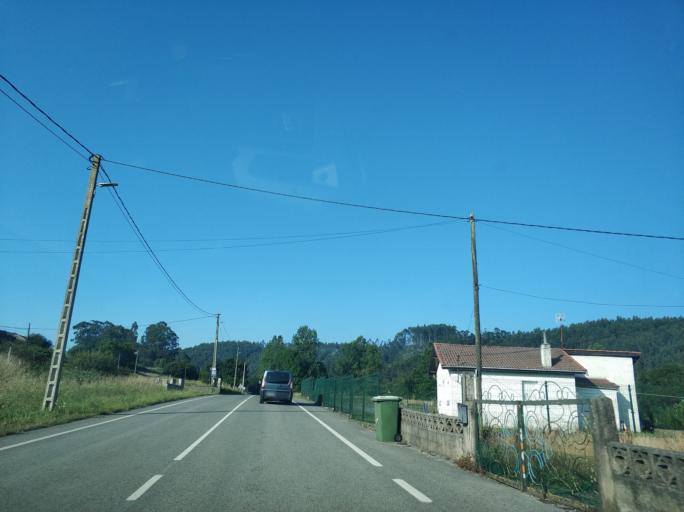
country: ES
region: Cantabria
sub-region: Provincia de Cantabria
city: Polanco
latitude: 43.3855
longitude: -3.9668
